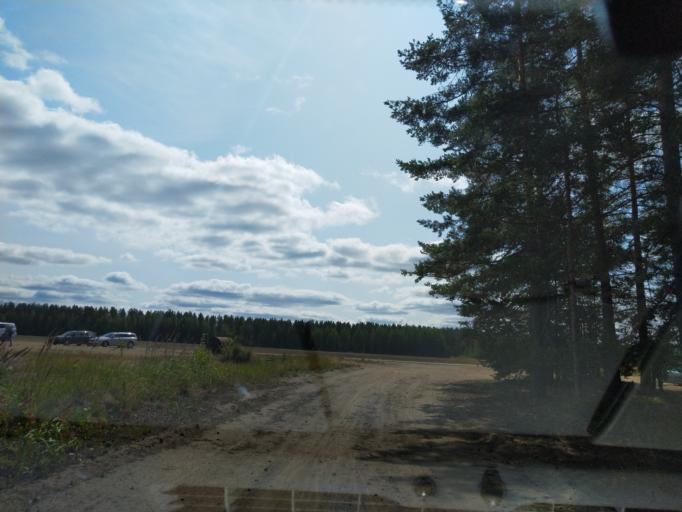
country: FI
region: Uusimaa
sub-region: Helsinki
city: Kaerkoelae
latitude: 60.7443
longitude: 24.1027
